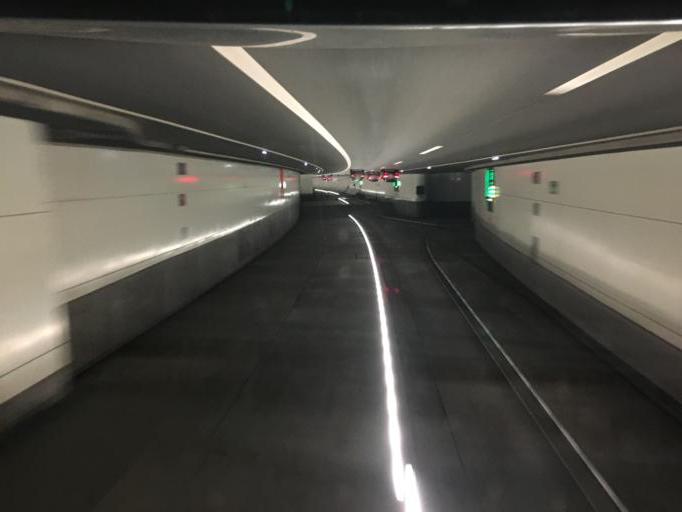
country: CH
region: Zurich
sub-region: Bezirk Affoltern
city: Wettswil / Wettswil (Dorf)
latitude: 47.3448
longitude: 8.4709
